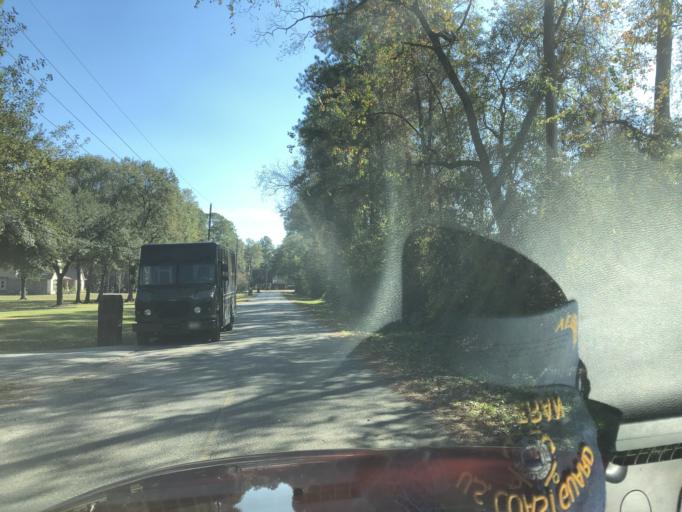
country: US
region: Texas
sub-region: Harris County
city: Tomball
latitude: 30.0314
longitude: -95.5426
